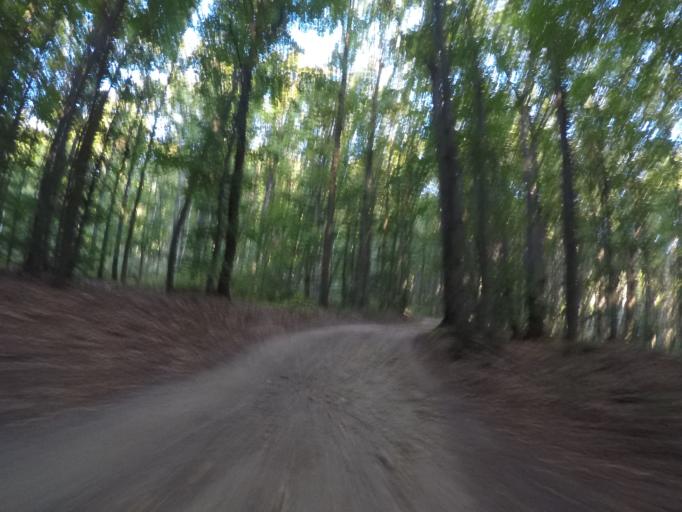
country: SK
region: Kosicky
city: Kosice
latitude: 48.7452
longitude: 21.1920
